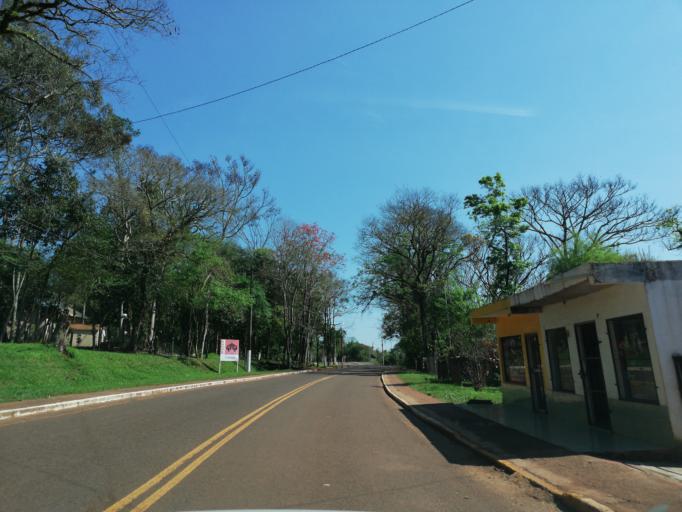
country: AR
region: Misiones
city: Puerto Eldorado
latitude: -26.4109
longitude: -54.6888
